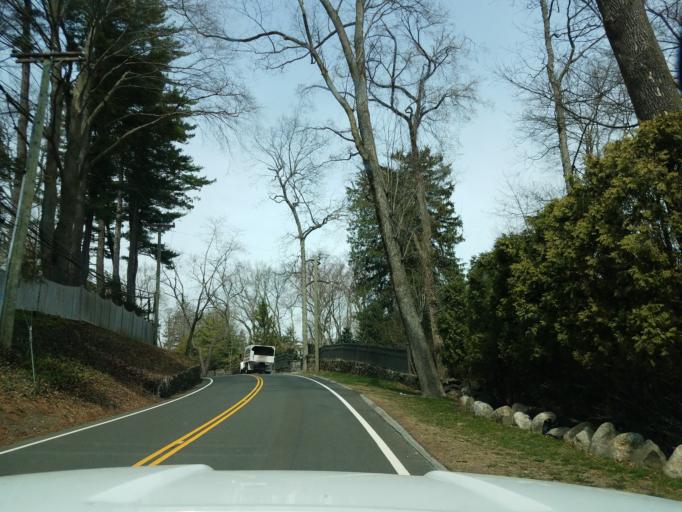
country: US
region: Connecticut
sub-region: Fairfield County
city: Greenwich
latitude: 41.0325
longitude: -73.6422
